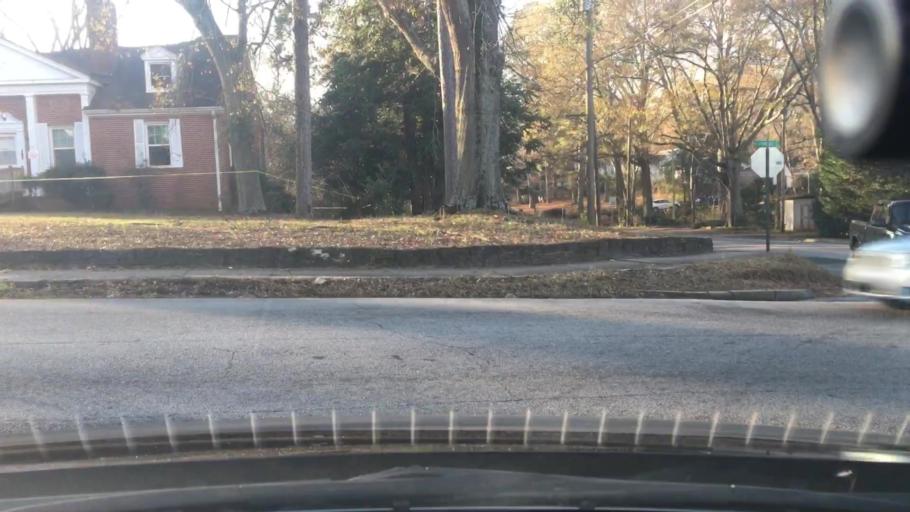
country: US
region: Georgia
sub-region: Spalding County
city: Experiment
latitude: 33.2459
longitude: -84.2868
